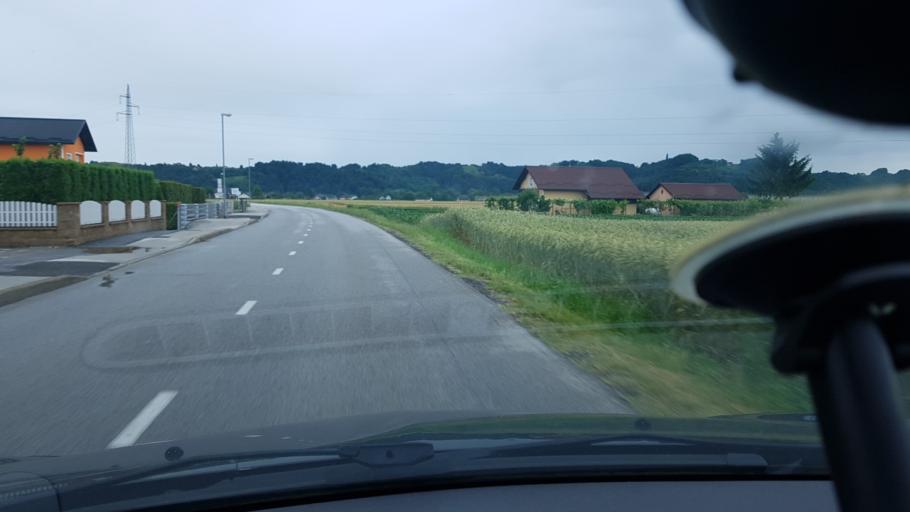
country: SI
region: Videm
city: Videm pri Ptuju
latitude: 46.3777
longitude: 15.8843
